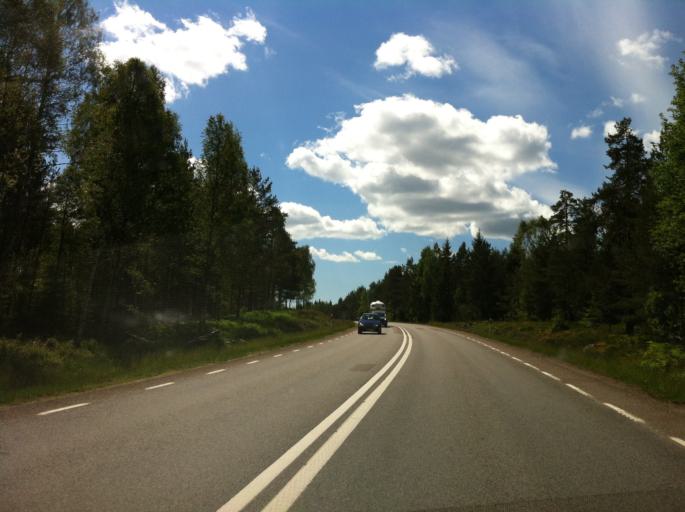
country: SE
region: Vaestra Goetaland
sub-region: Amals Kommun
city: Amal
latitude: 59.0363
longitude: 12.6710
